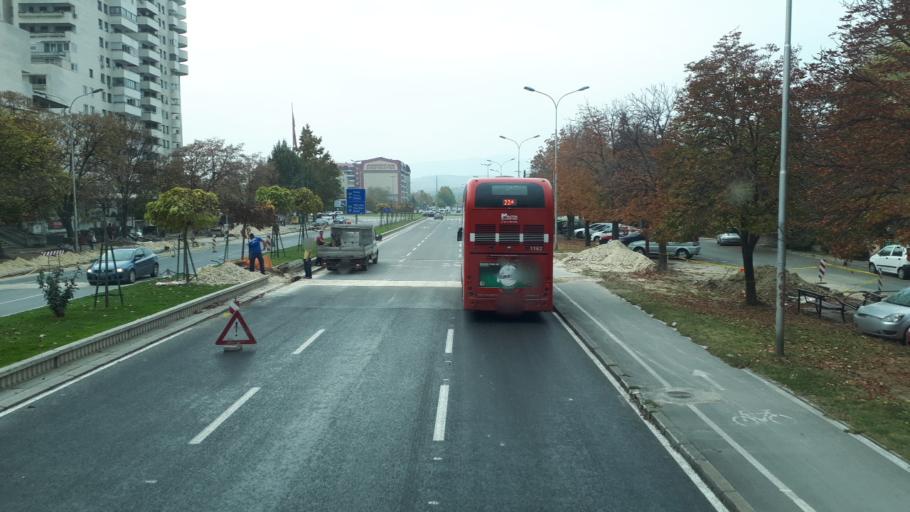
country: MK
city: Krushopek
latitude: 42.0081
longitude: 21.3706
